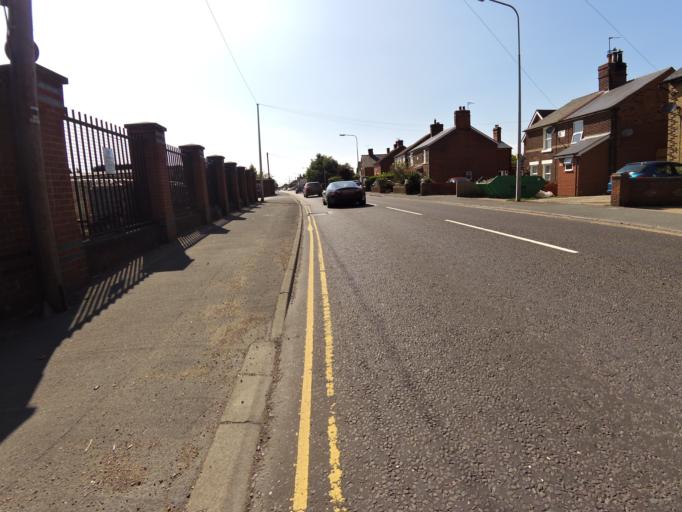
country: GB
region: England
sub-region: Essex
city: Eight Ash Green
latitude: 51.8891
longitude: 0.8450
